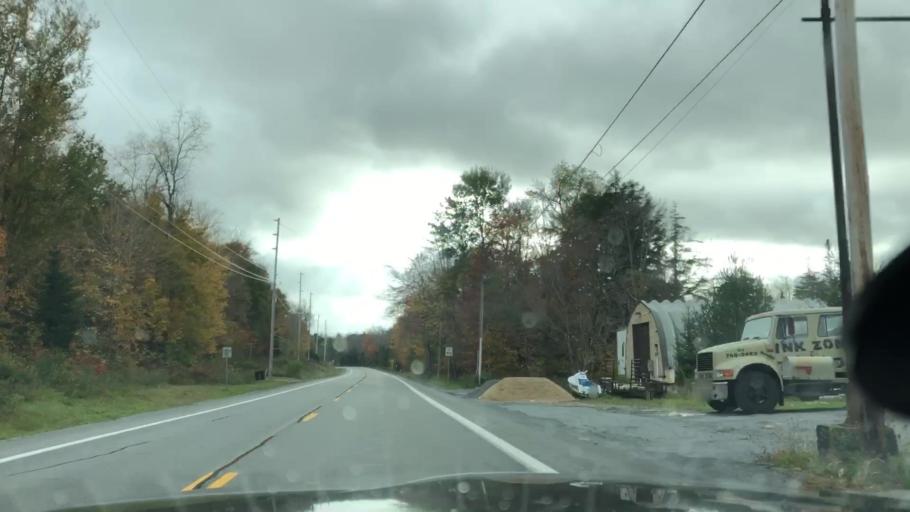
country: US
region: New York
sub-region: Oneida County
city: Boonville
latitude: 43.5843
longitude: -75.1201
